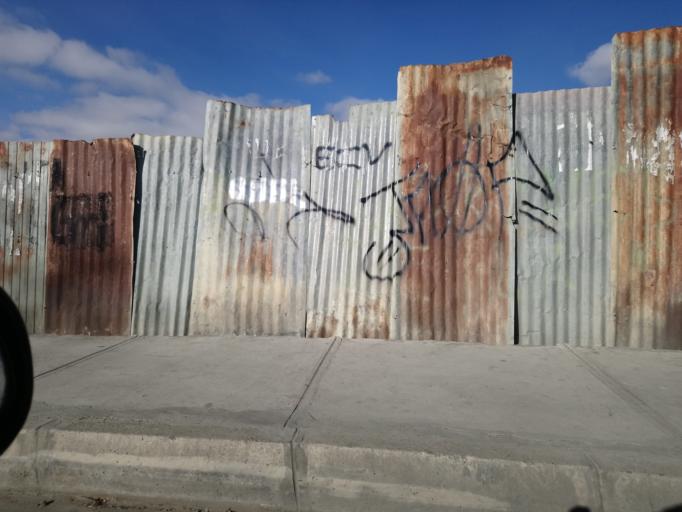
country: BO
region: La Paz
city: La Paz
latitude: -16.5098
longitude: -68.1134
